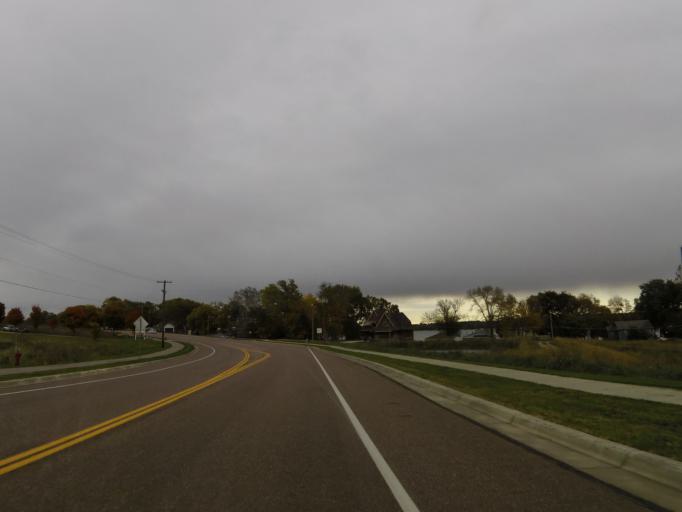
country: US
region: Minnesota
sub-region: Scott County
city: Prior Lake
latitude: 44.7036
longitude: -93.4892
